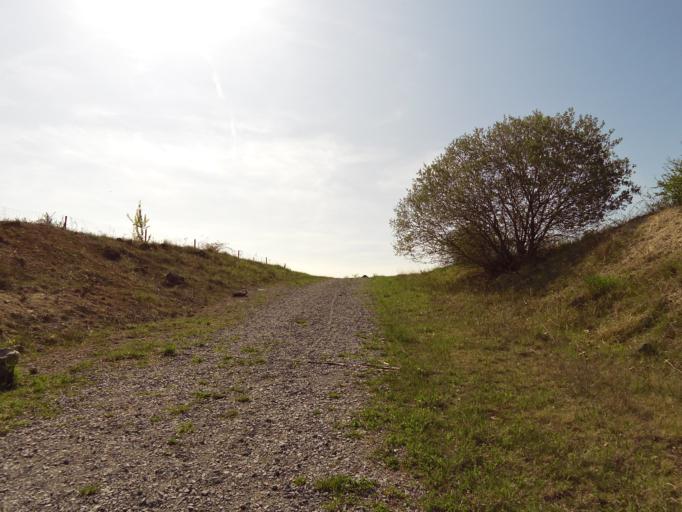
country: DE
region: Rheinland-Pfalz
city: Gollheim
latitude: 49.6024
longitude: 8.0473
